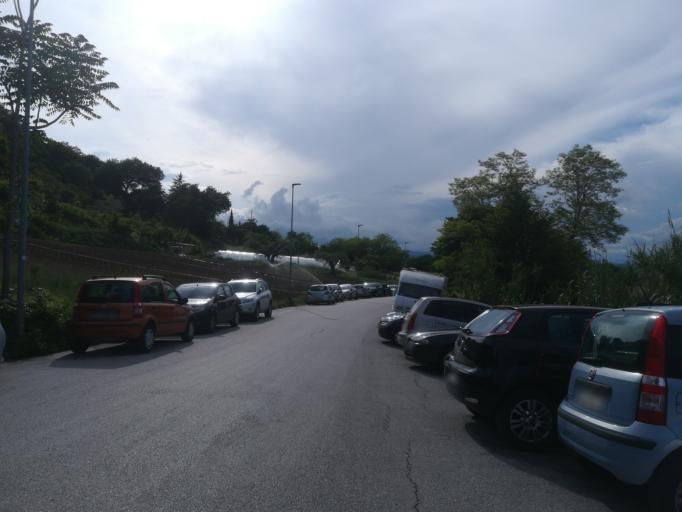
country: IT
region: The Marches
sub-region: Provincia di Macerata
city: Macerata
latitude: 43.3022
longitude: 13.4555
